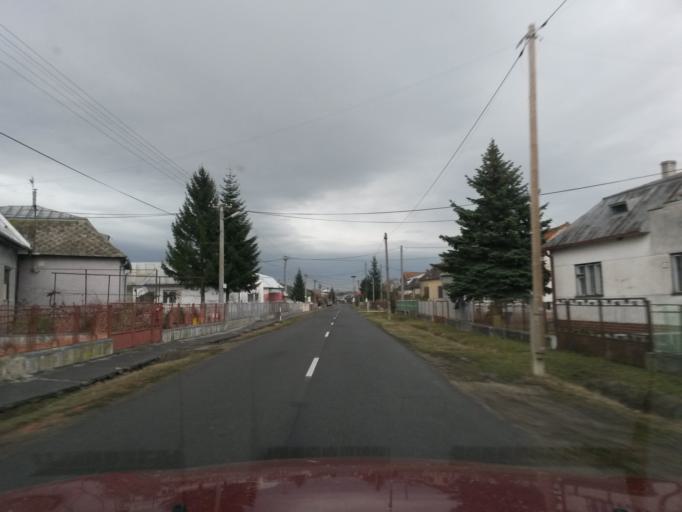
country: SK
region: Kosicky
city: Michalovce
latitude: 48.6642
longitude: 22.0196
